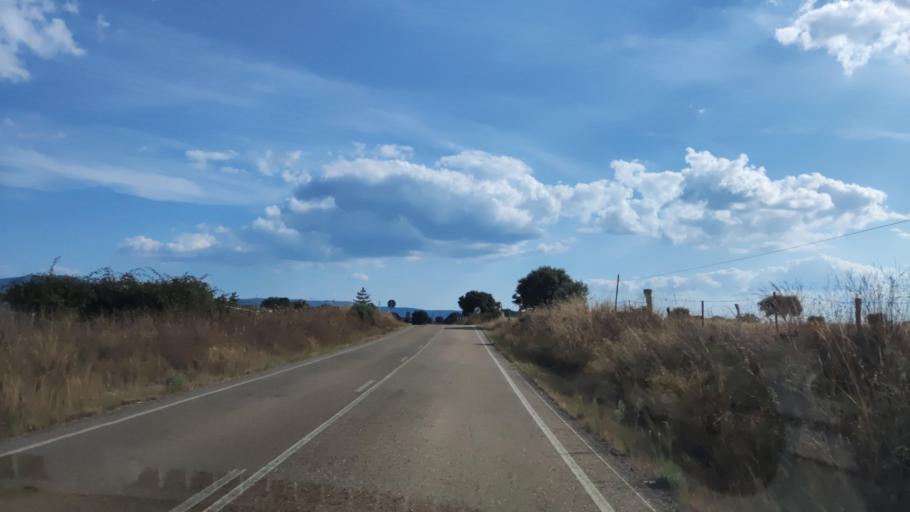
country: ES
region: Castille and Leon
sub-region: Provincia de Salamanca
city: Martiago
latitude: 40.4629
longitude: -6.4901
